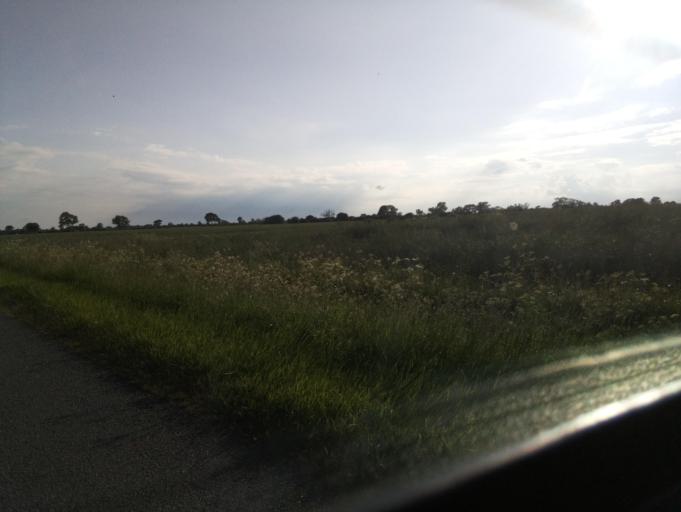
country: GB
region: England
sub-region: Lincolnshire
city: Navenby
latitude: 53.1078
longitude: -0.6034
